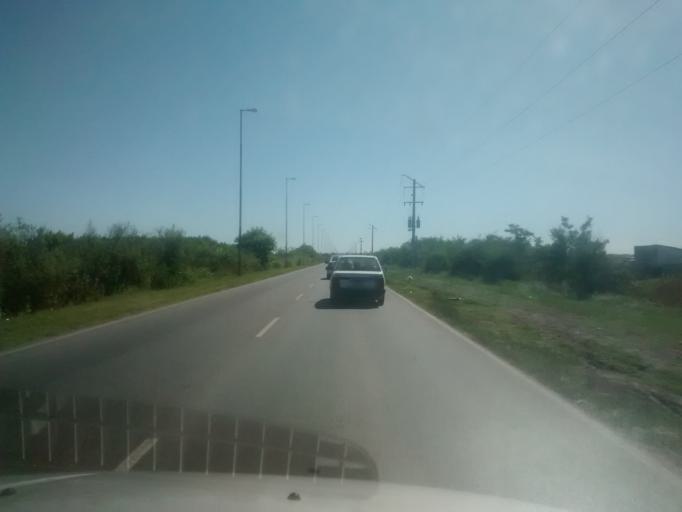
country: AR
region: Buenos Aires
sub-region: Partido de Berisso
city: Berisso
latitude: -34.8932
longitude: -57.8762
